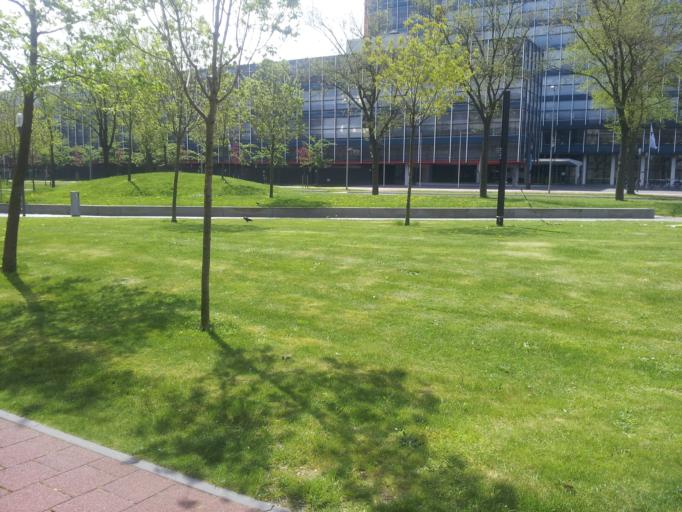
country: NL
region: South Holland
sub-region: Gemeente Delft
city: Delft
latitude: 51.9992
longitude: 4.3738
